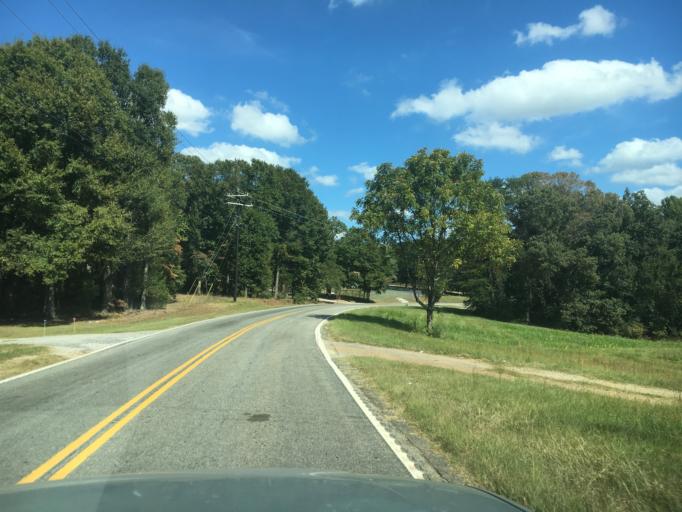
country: US
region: South Carolina
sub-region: Spartanburg County
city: Duncan
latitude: 34.8978
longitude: -82.1261
